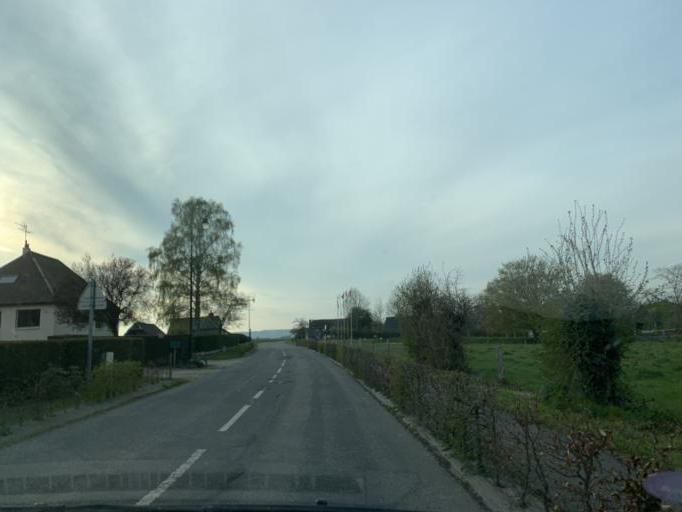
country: FR
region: Haute-Normandie
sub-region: Departement de la Seine-Maritime
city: La Mailleraye-sur-Seine
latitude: 49.4967
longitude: 0.7598
